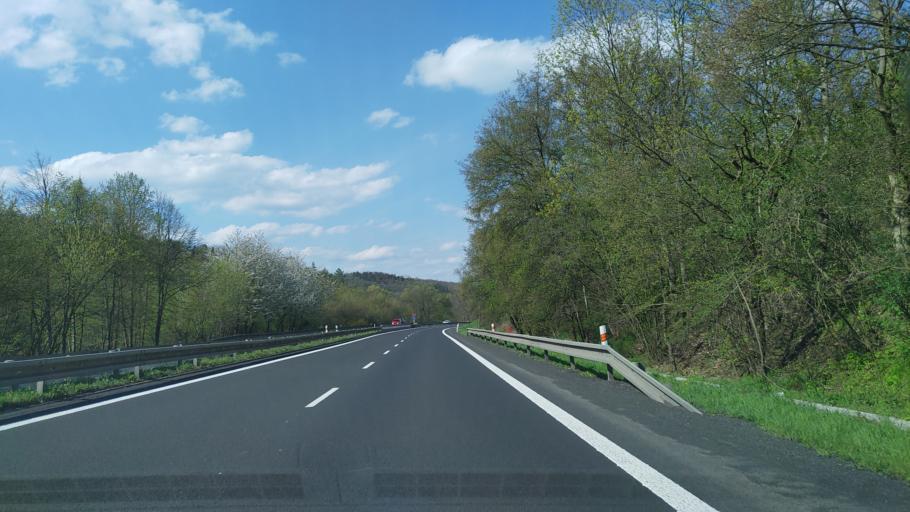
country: CZ
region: Ustecky
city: Bilina Kyselka
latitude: 50.5346
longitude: 13.7586
